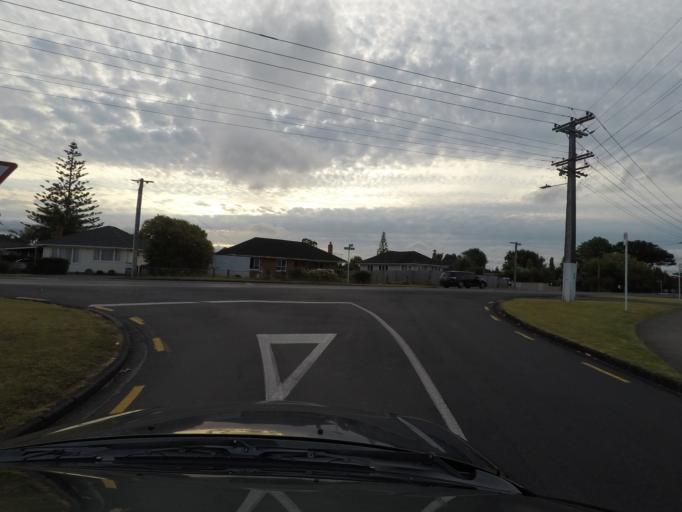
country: NZ
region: Auckland
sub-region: Auckland
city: Rosebank
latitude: -36.8339
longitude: 174.6496
